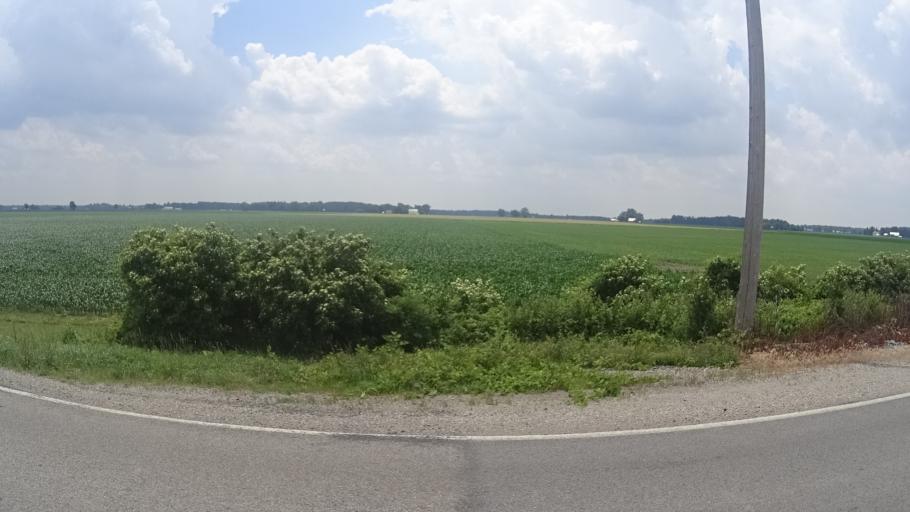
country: US
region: Ohio
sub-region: Erie County
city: Milan
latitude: 41.3227
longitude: -82.6454
